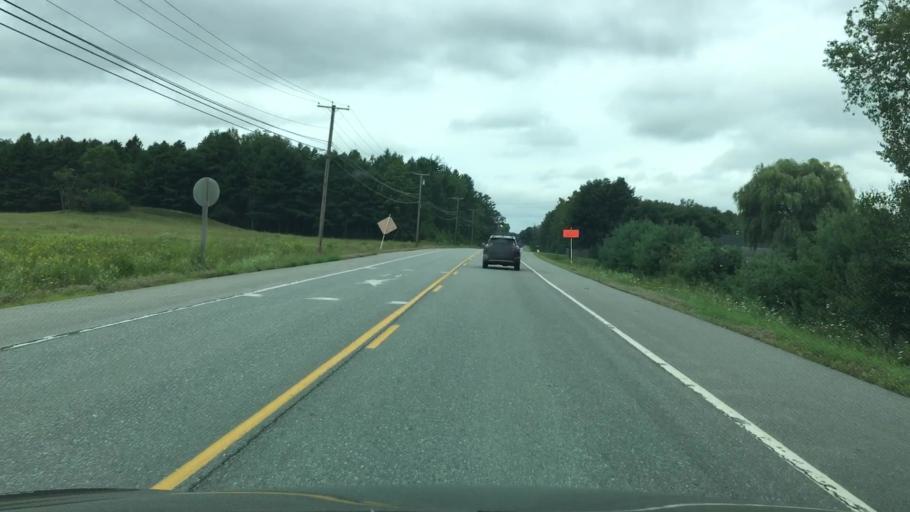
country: US
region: Maine
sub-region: Penobscot County
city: Orrington
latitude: 44.7037
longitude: -68.8225
